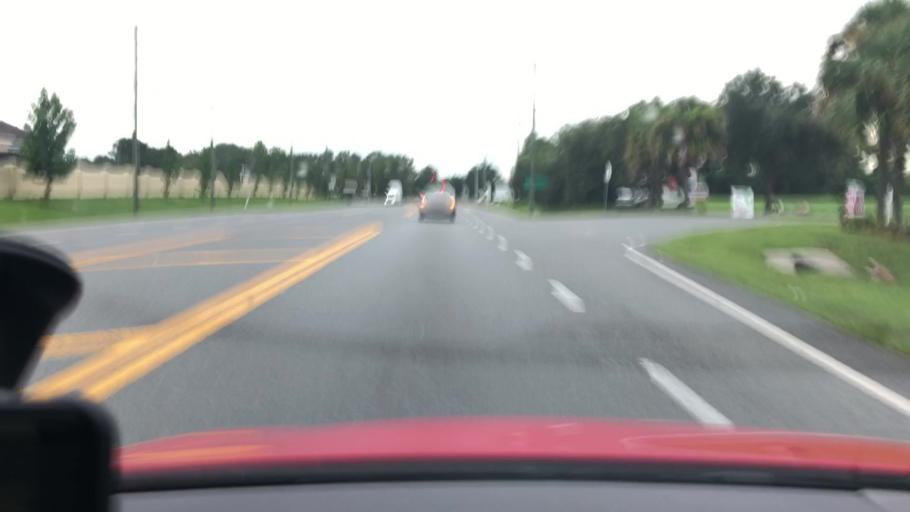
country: US
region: Florida
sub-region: Lake County
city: Mount Dora
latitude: 28.8495
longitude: -81.6338
